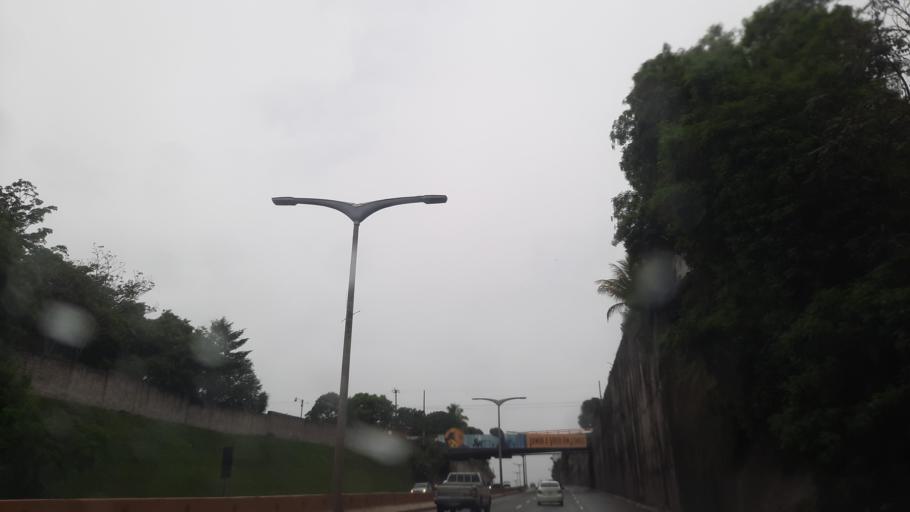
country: SV
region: La Libertad
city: Santa Tecla
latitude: 13.6854
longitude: -89.2828
